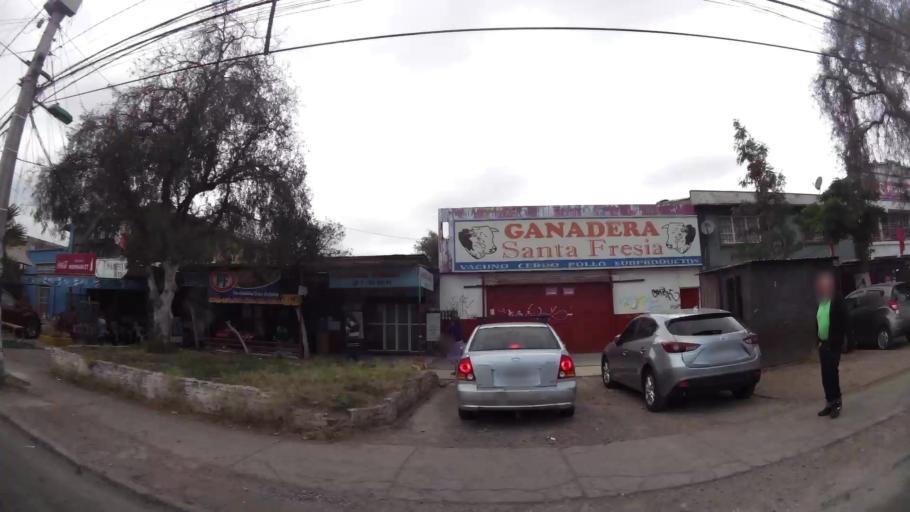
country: CL
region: Santiago Metropolitan
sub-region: Provincia de Santiago
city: Santiago
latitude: -33.5059
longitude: -70.6919
